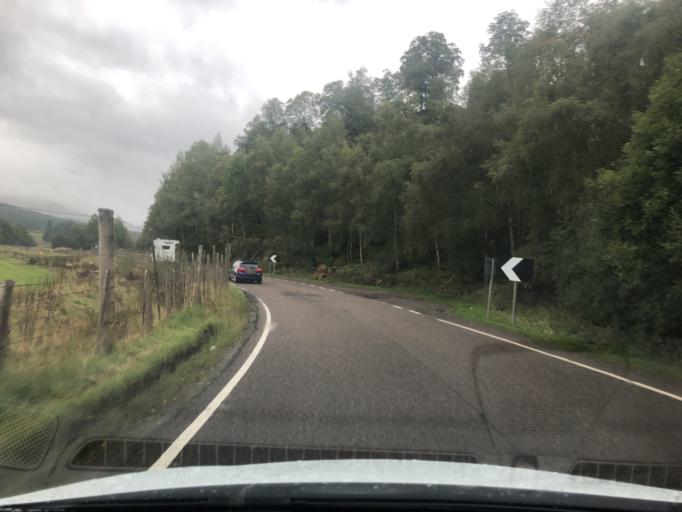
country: GB
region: Scotland
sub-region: Highland
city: Kingussie
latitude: 56.9782
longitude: -4.3776
